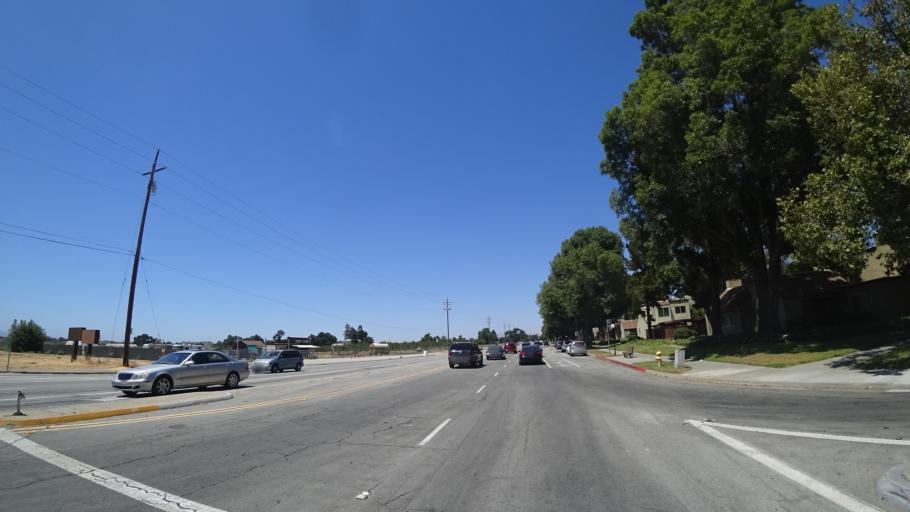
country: US
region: California
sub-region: Santa Clara County
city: Seven Trees
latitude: 37.2588
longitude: -121.8308
